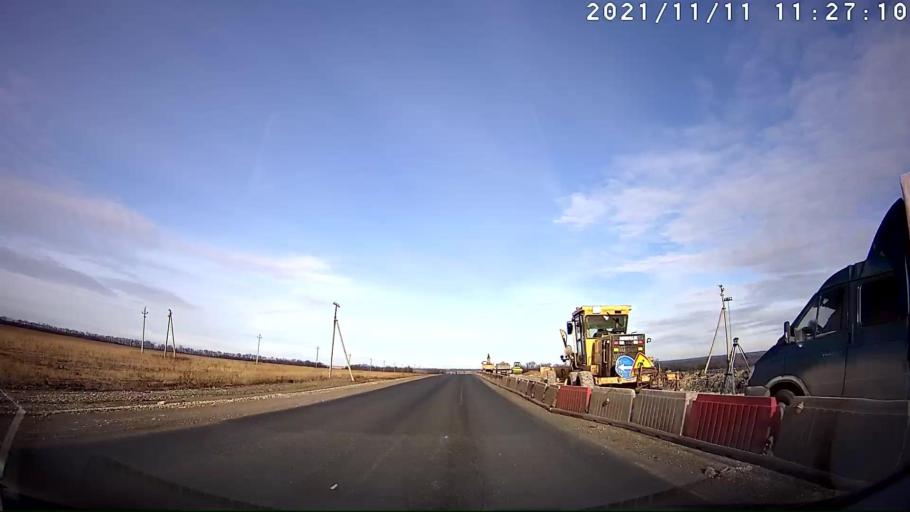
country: RU
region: Samara
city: Varlamovo
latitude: 53.2442
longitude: 48.4867
